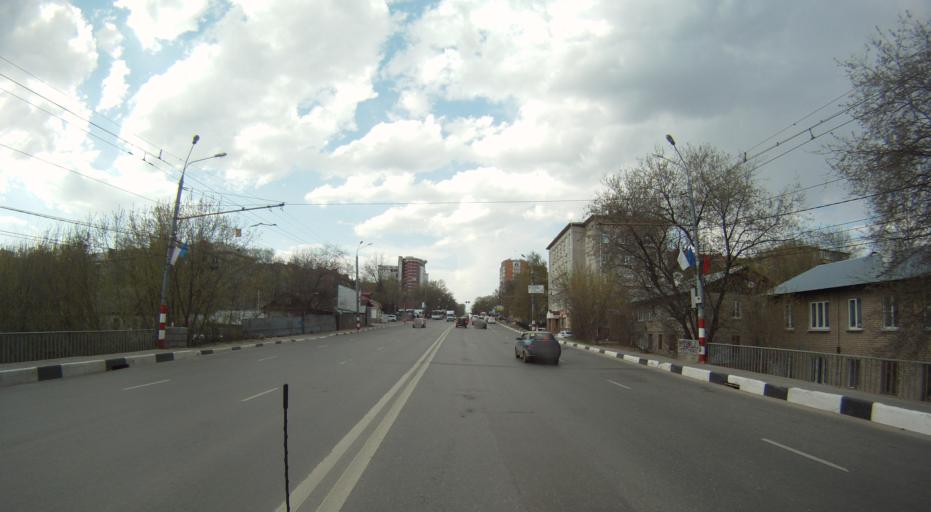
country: RU
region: Nizjnij Novgorod
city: Nizhniy Novgorod
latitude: 56.3069
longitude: 44.0248
